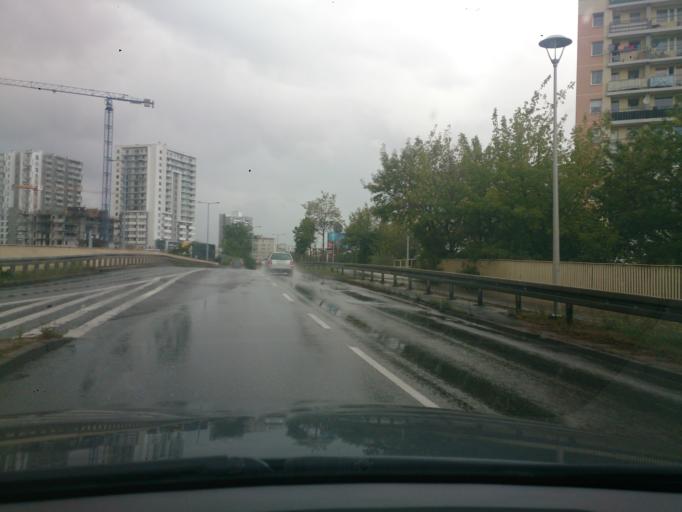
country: PL
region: Pomeranian Voivodeship
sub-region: Sopot
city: Sopot
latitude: 54.4000
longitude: 18.5936
